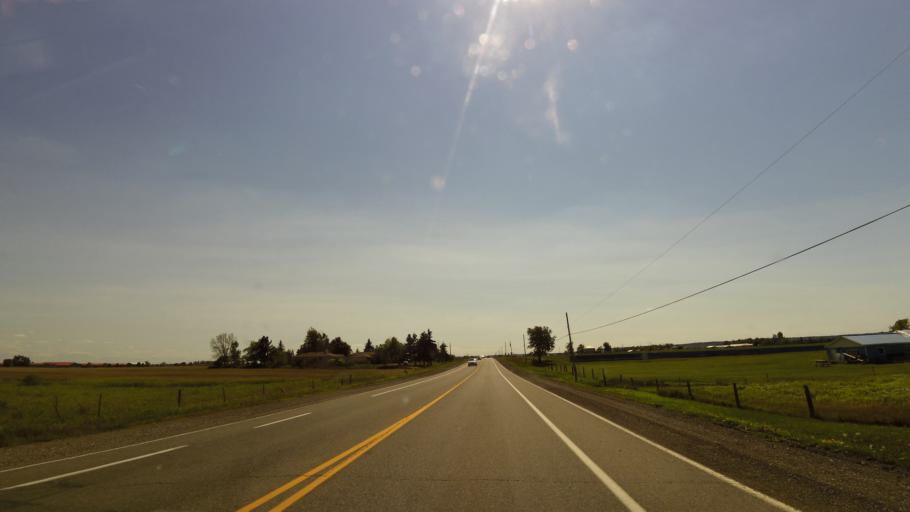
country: CA
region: Ontario
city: Brampton
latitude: 43.7697
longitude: -79.8824
